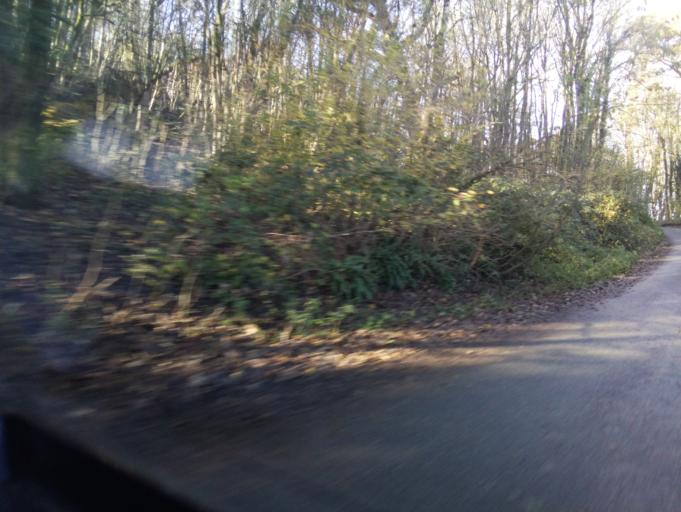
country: GB
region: England
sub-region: Dorset
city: Sherborne
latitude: 50.8469
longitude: -2.4929
